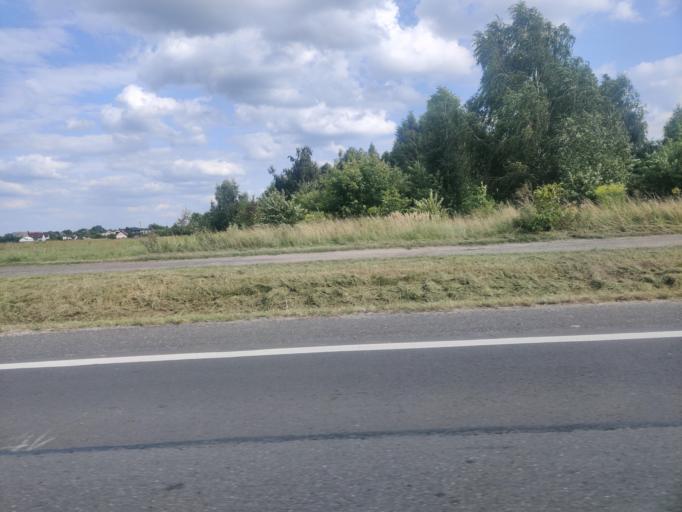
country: PL
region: Greater Poland Voivodeship
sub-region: Konin
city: Konin
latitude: 52.1984
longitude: 18.2690
